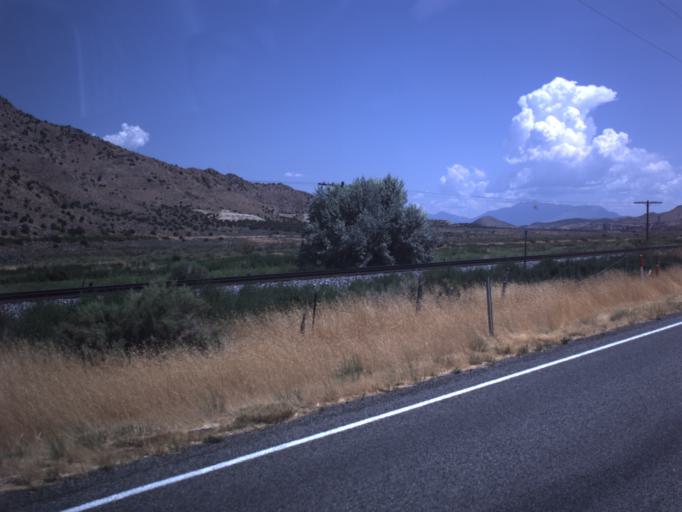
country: US
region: Utah
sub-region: Millard County
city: Delta
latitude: 39.5379
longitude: -112.2584
